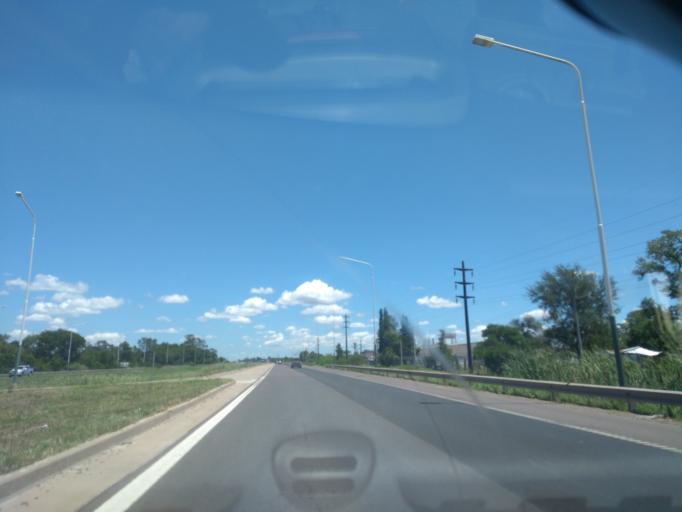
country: AR
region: Chaco
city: Fontana
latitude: -27.3906
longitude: -59.0259
